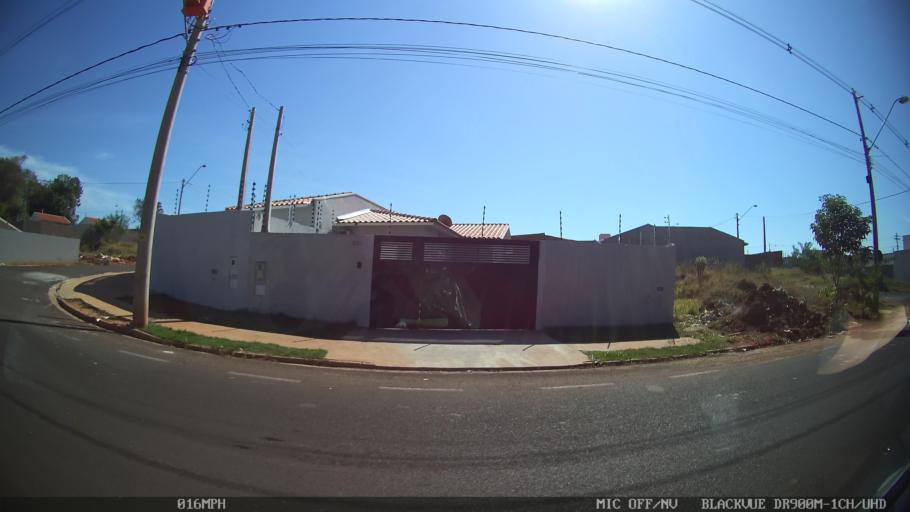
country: BR
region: Sao Paulo
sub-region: Sao Jose Do Rio Preto
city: Sao Jose do Rio Preto
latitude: -20.7608
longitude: -49.4220
